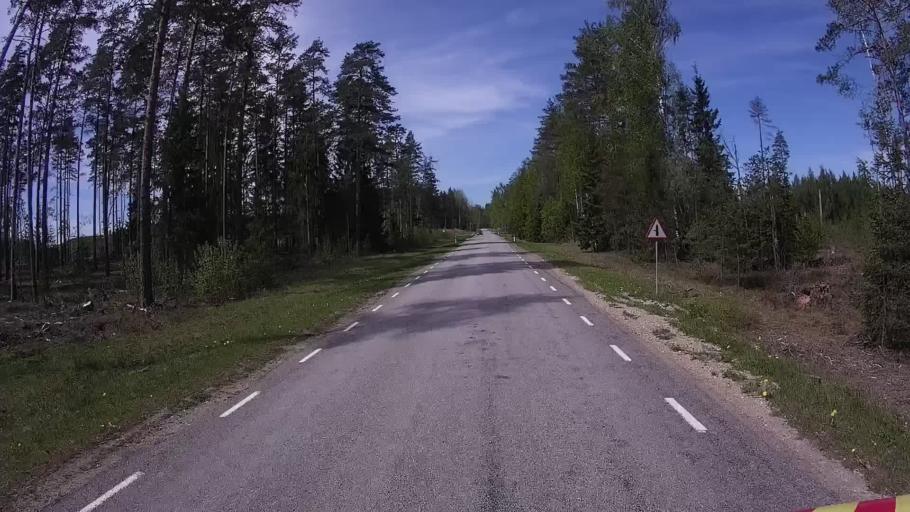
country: EE
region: Vorumaa
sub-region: Antsla vald
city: Vana-Antsla
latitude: 57.6195
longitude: 26.3534
